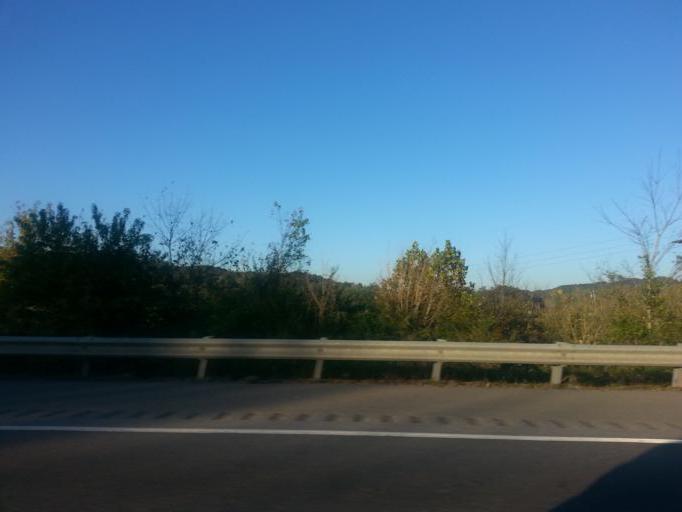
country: US
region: Tennessee
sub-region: Anderson County
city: Norris
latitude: 36.1397
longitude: -84.0445
